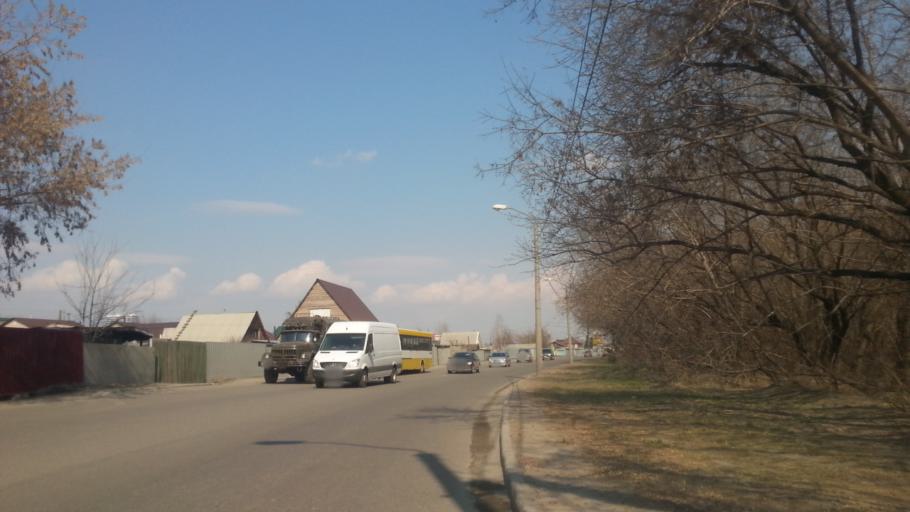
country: RU
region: Altai Krai
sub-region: Gorod Barnaulskiy
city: Barnaul
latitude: 53.3220
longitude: 83.7647
